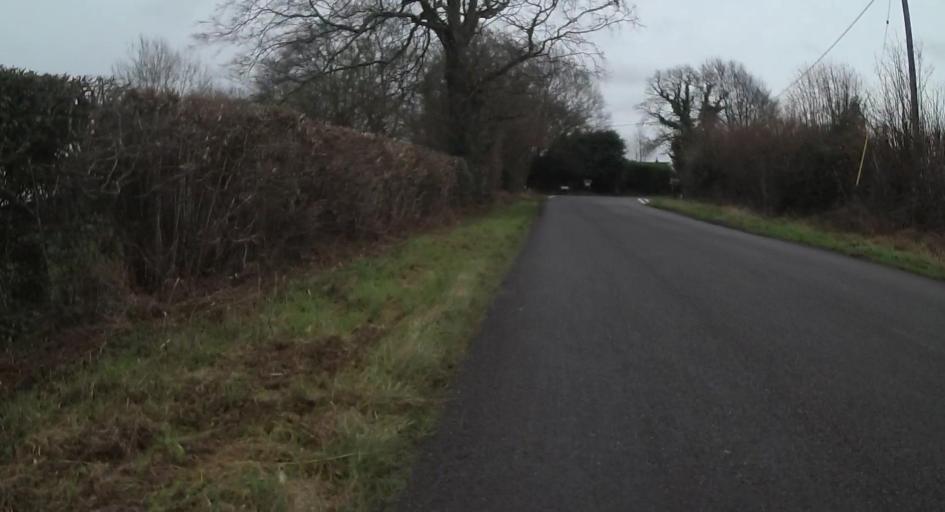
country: GB
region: England
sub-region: Hampshire
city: Four Marks
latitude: 51.1054
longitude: -1.0249
